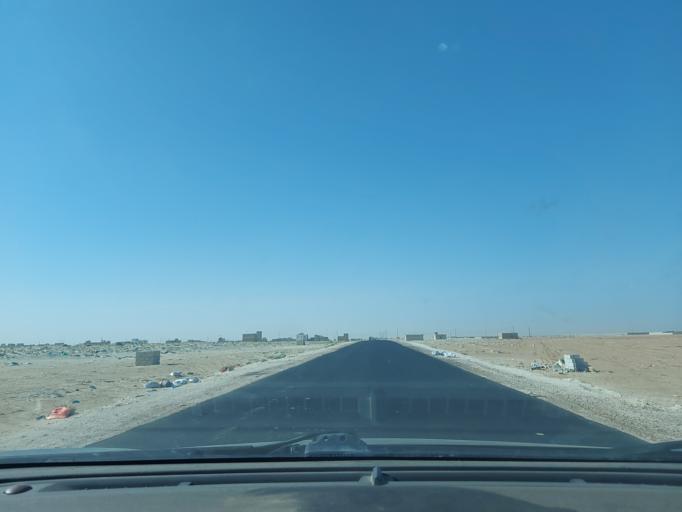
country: MR
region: Nouakchott
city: Nouakchott
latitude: 17.9990
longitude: -15.9882
